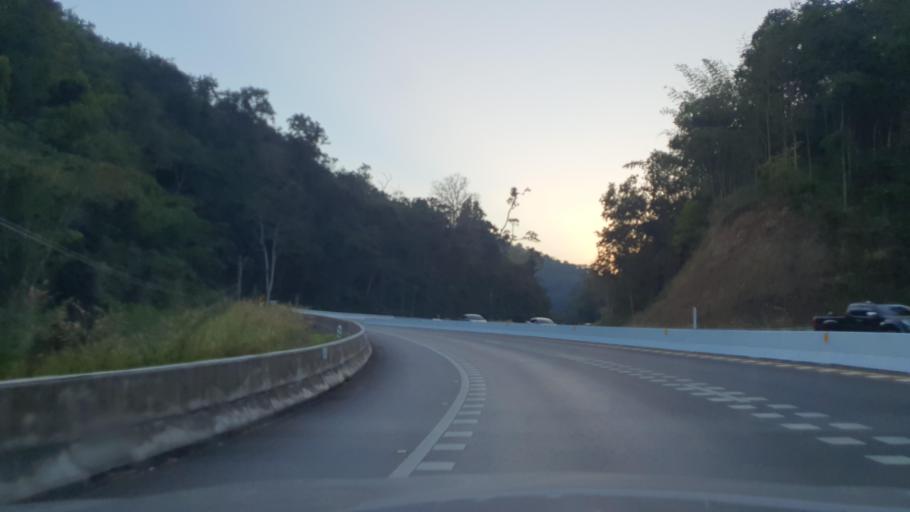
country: TH
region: Lampang
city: Wang Nuea
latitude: 19.0927
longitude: 99.4218
